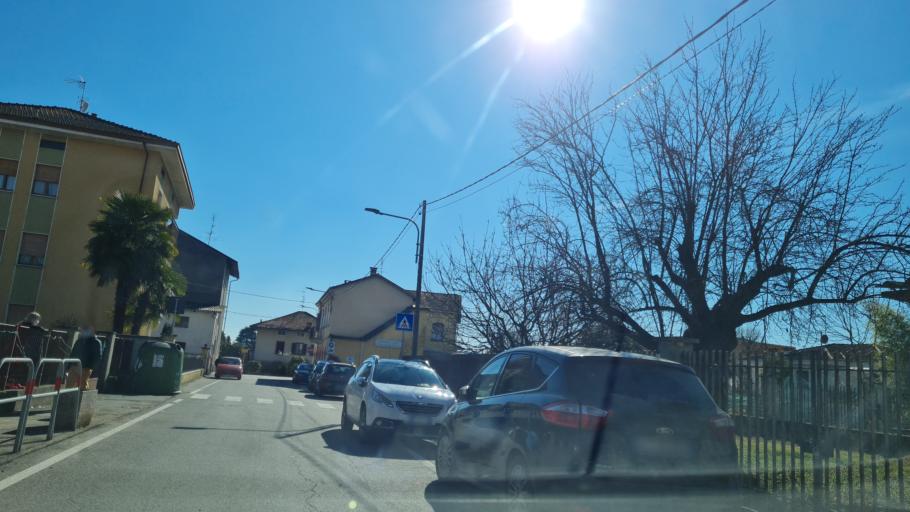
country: IT
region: Piedmont
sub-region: Provincia di Biella
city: Vergnasco
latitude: 45.4877
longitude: 8.0796
